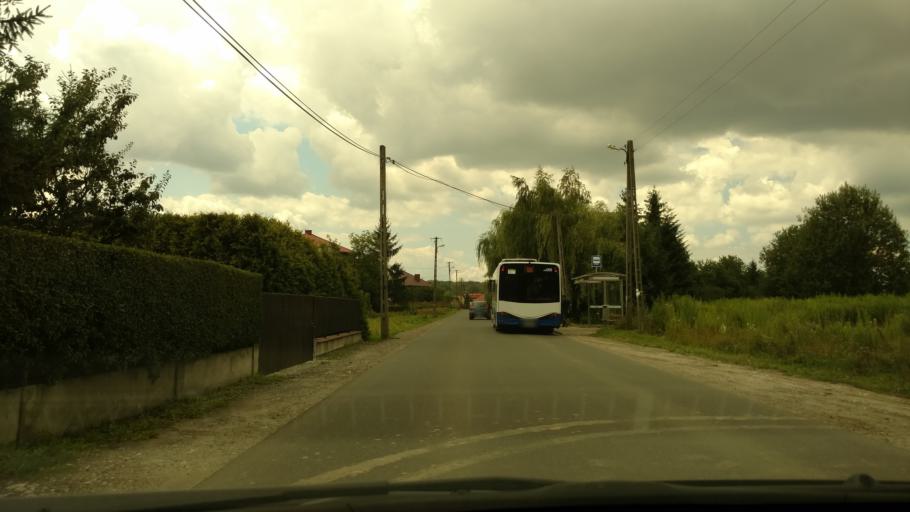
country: PL
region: Lesser Poland Voivodeship
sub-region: Powiat krakowski
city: Zielonki
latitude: 50.1120
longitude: 19.8937
